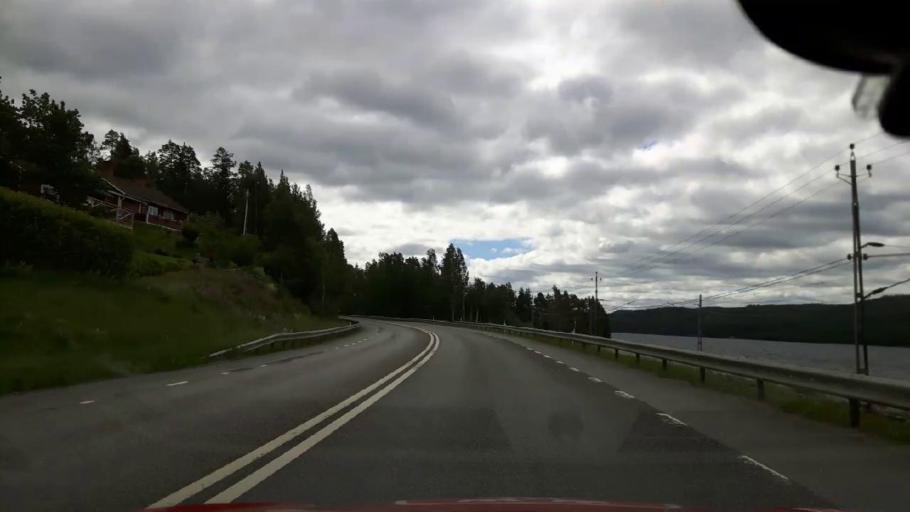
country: SE
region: Jaemtland
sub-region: Braecke Kommun
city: Braecke
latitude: 62.7408
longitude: 15.4271
